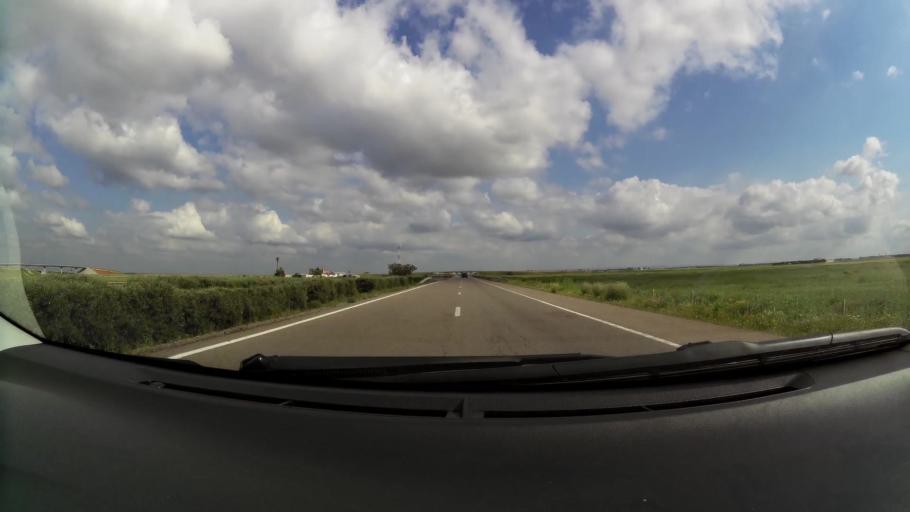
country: MA
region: Chaouia-Ouardigha
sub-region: Settat Province
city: Berrechid
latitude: 33.2952
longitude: -7.5550
